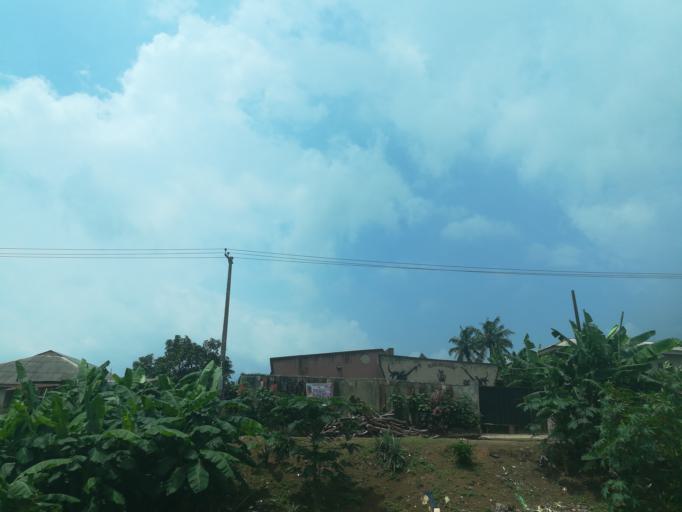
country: NG
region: Lagos
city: Ikorodu
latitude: 6.6712
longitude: 3.6685
